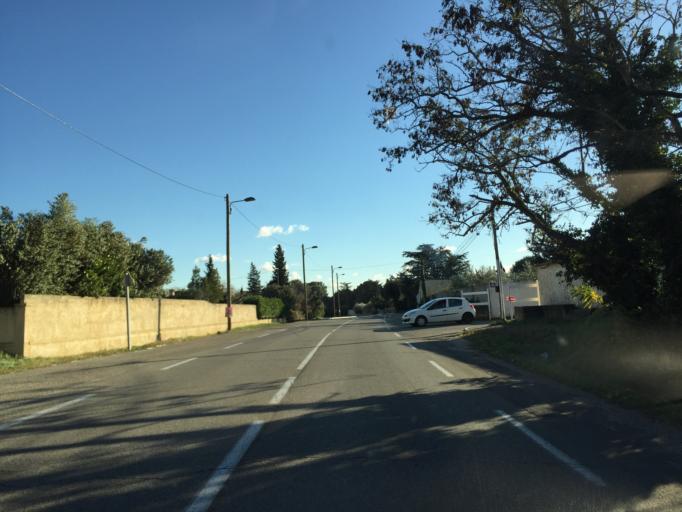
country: FR
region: Provence-Alpes-Cote d'Azur
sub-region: Departement du Vaucluse
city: Sorgues
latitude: 44.0267
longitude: 4.8638
